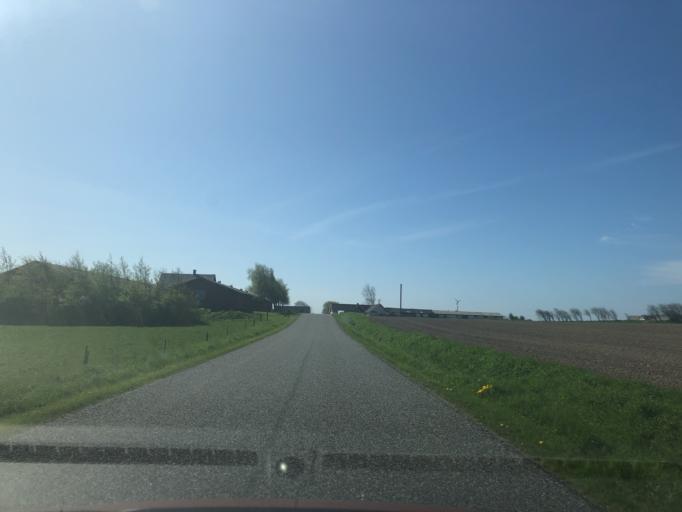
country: DK
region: Central Jutland
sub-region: Holstebro Kommune
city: Vinderup
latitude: 56.5846
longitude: 8.7735
